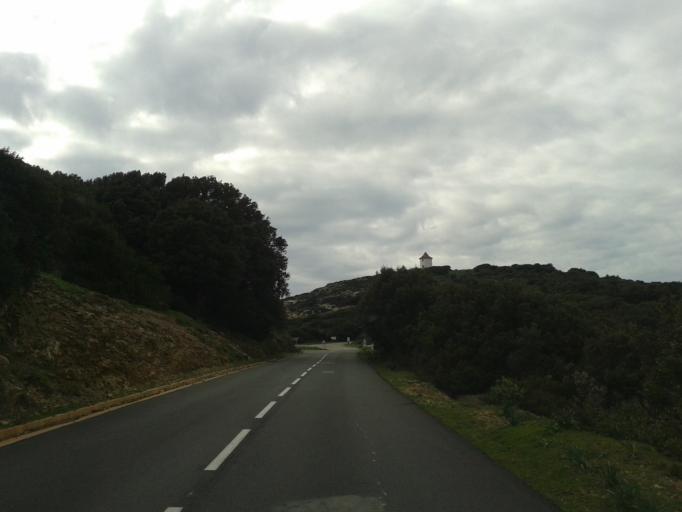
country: FR
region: Corsica
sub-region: Departement de la Haute-Corse
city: Brando
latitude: 42.9733
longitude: 9.3685
